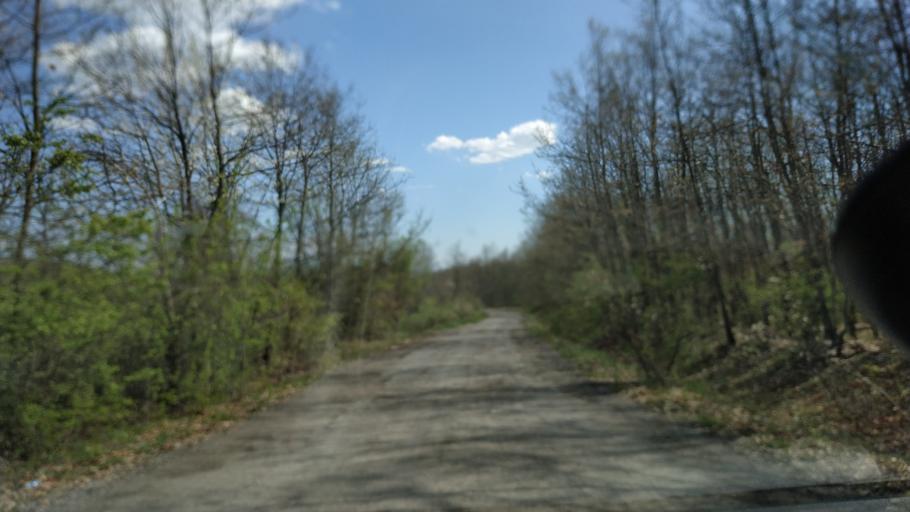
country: RS
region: Central Serbia
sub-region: Zajecarski Okrug
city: Soko Banja
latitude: 43.5408
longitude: 21.9036
